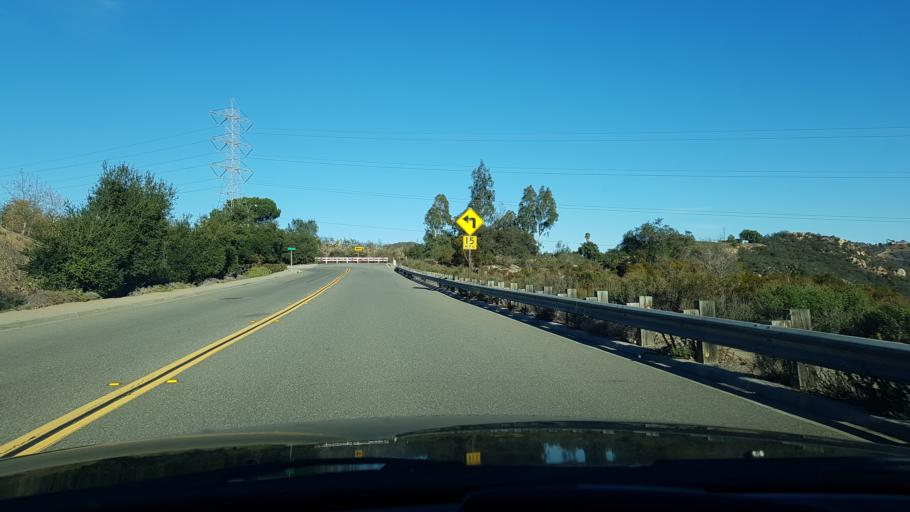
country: US
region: California
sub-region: San Diego County
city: Hidden Meadows
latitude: 33.2144
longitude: -117.0963
